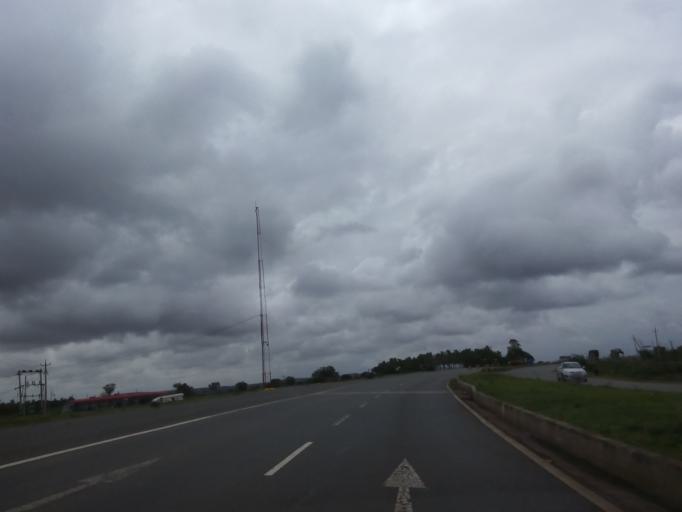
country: IN
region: Karnataka
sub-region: Haveri
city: Haveri
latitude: 14.7734
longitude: 75.4202
